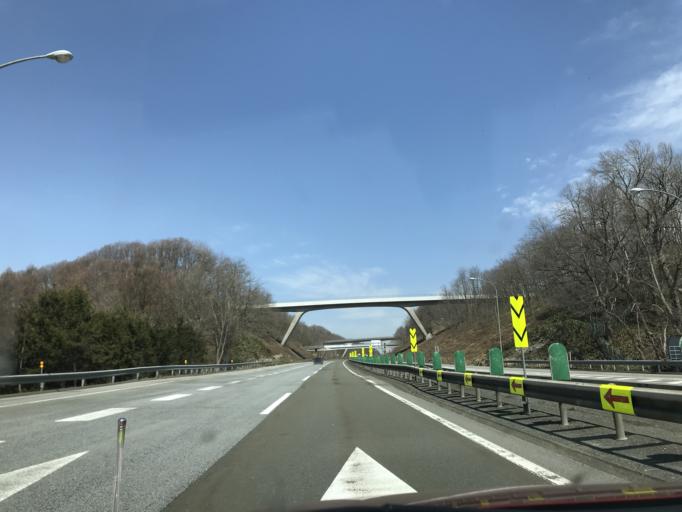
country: JP
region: Hokkaido
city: Bibai
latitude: 43.2458
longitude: 141.8303
